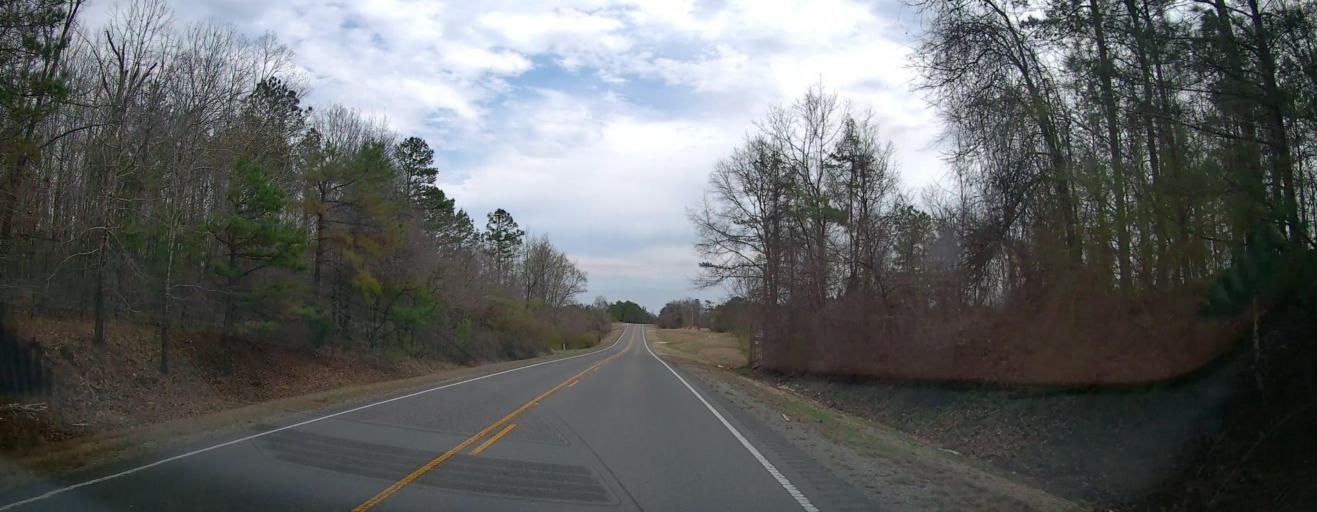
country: US
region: Alabama
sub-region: Marion County
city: Guin
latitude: 34.0324
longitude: -87.9454
